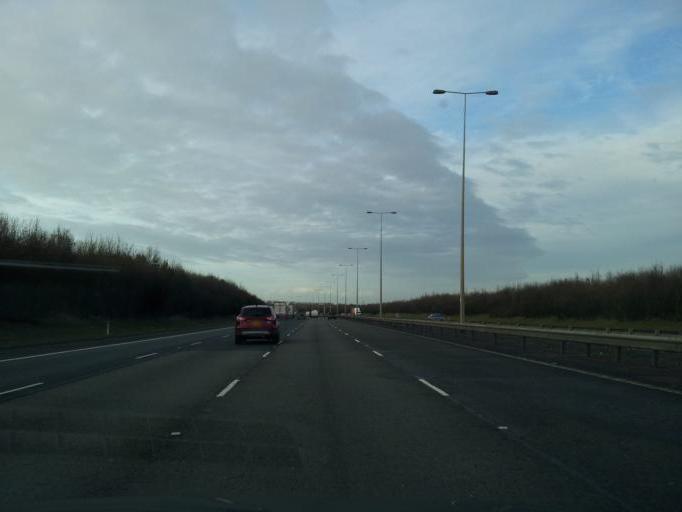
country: GB
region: England
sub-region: Cambridgeshire
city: Stilton
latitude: 52.4833
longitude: -0.2862
